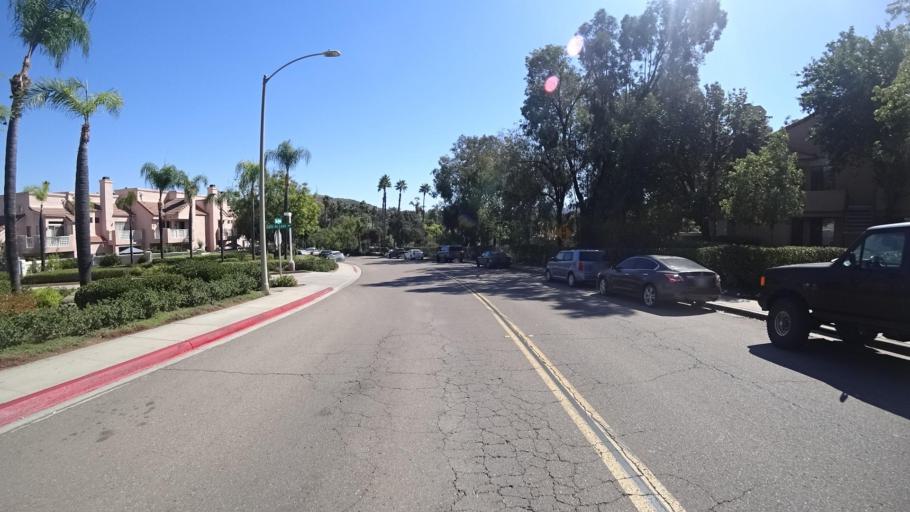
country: US
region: California
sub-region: San Diego County
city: Rancho San Diego
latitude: 32.7534
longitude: -116.9289
